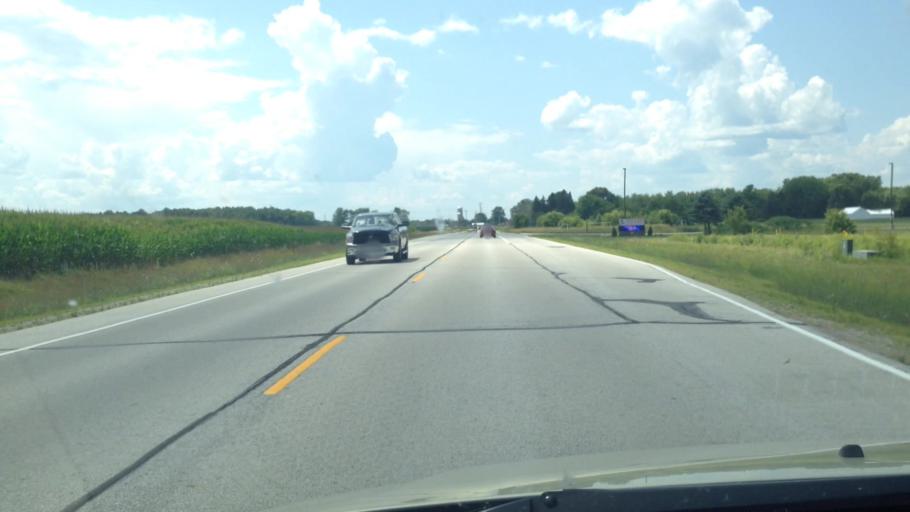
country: US
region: Wisconsin
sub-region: Brown County
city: Pulaski
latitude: 44.6567
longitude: -88.2367
